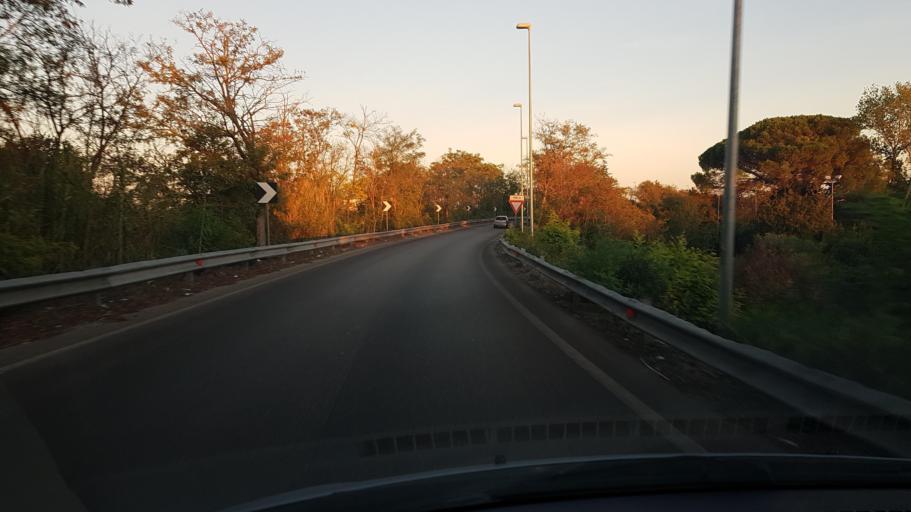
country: IT
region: Apulia
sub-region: Provincia di Lecce
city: Castromediano
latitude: 40.3226
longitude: 18.1848
